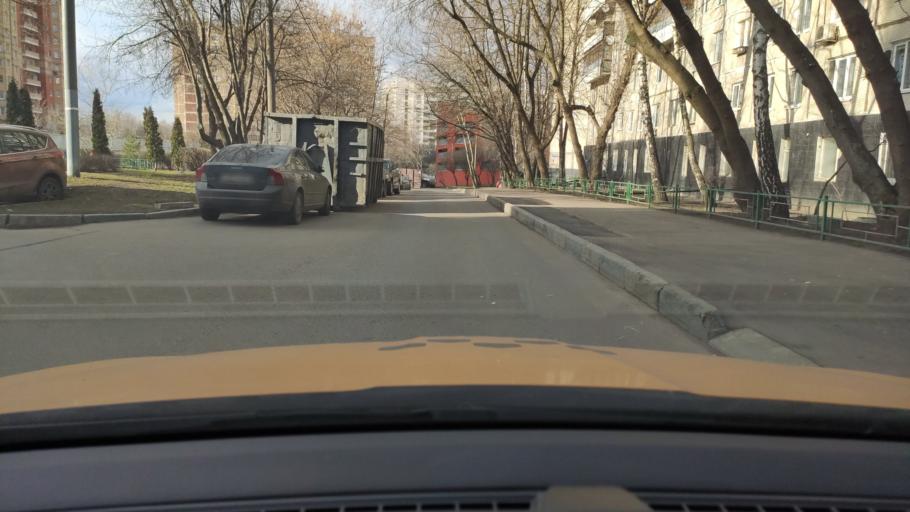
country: RU
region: Moscow
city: Orekhovo-Borisovo Severnoye
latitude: 55.6182
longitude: 37.6978
